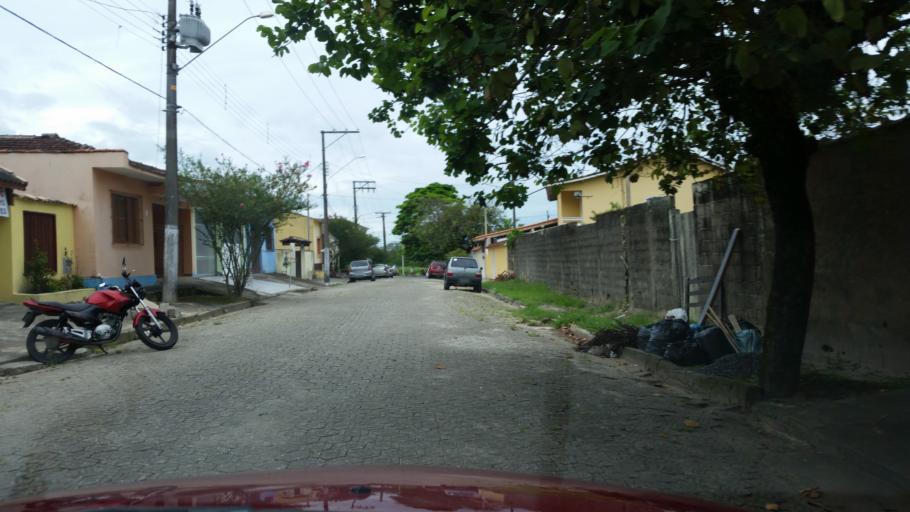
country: BR
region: Sao Paulo
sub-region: Iguape
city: Iguape
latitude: -24.7062
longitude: -47.5516
